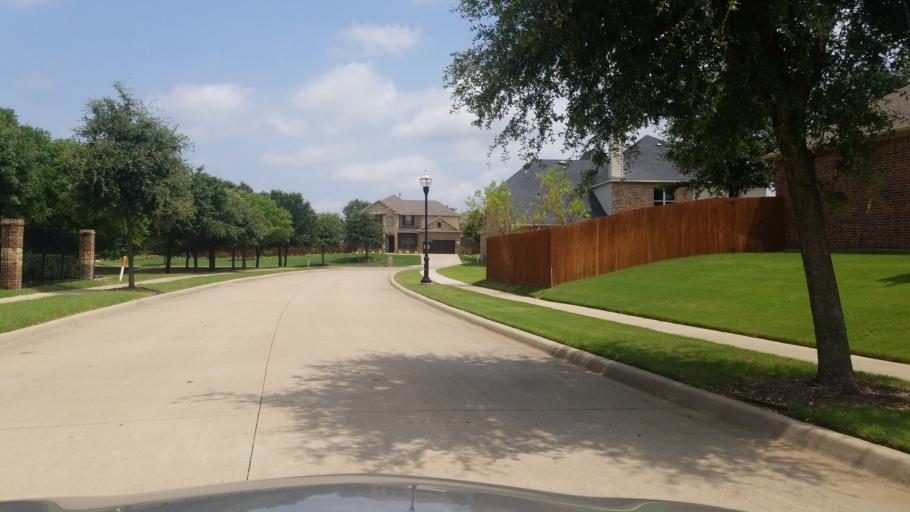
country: US
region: Texas
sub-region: Dallas County
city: Duncanville
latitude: 32.6837
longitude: -96.9374
